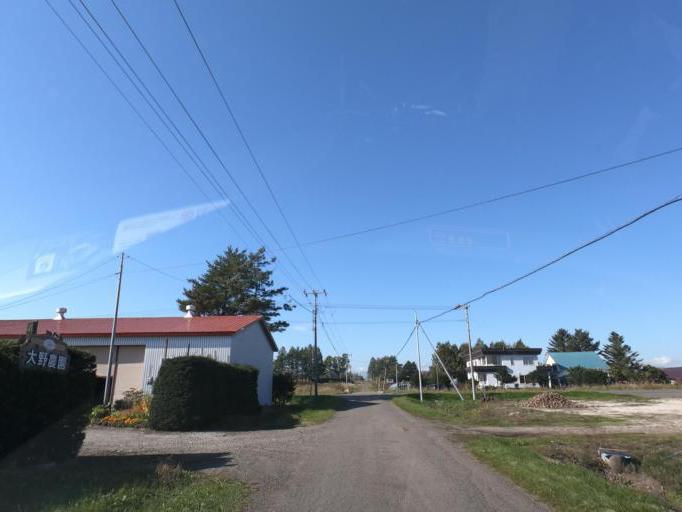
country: JP
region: Hokkaido
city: Obihiro
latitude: 42.9499
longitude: 143.2433
